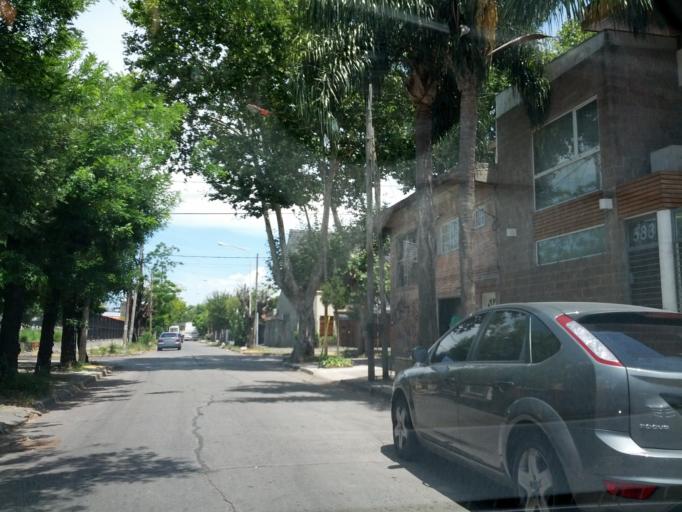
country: AR
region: Buenos Aires
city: San Justo
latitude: -34.6486
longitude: -58.5683
